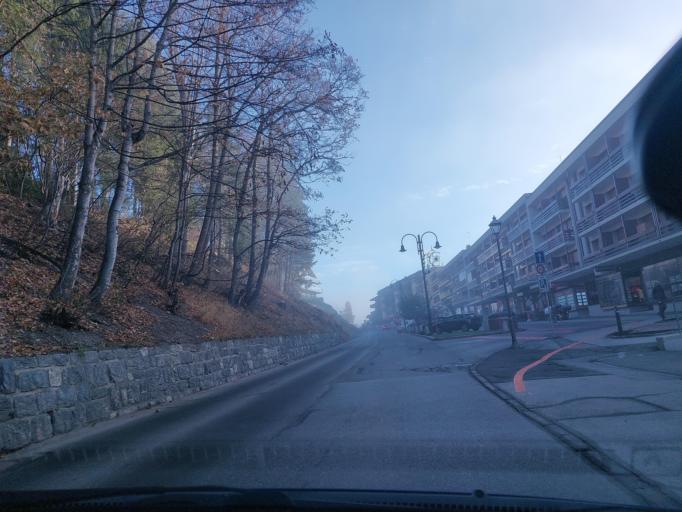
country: CH
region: Valais
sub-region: Sierre District
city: Montana
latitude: 46.3090
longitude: 7.4712
